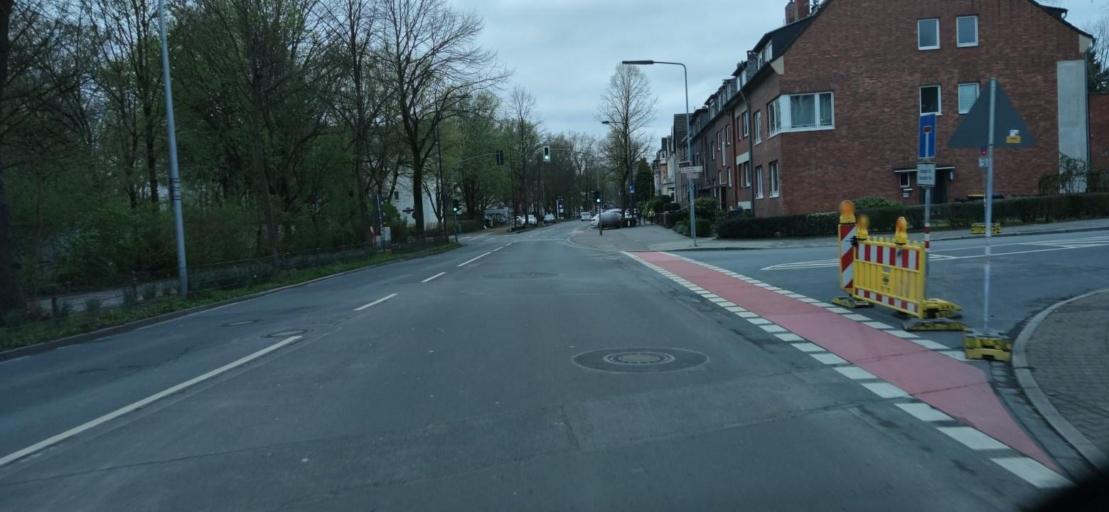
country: DE
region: North Rhine-Westphalia
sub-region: Regierungsbezirk Dusseldorf
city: Erkrath
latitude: 51.2014
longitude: 6.8489
